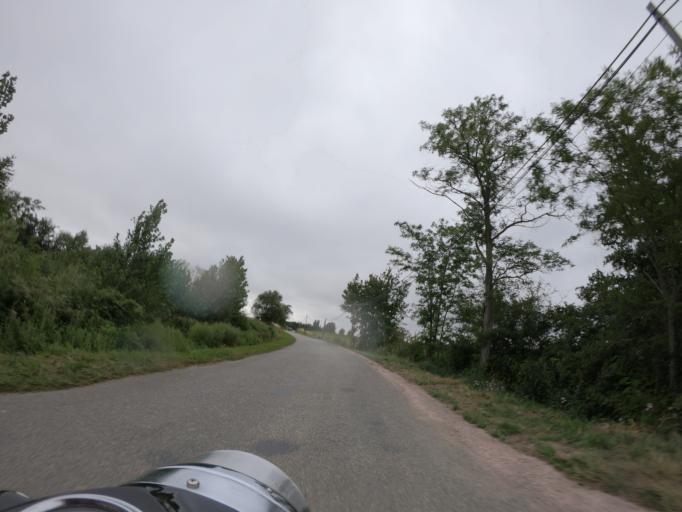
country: FR
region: Midi-Pyrenees
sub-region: Departement de l'Ariege
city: La Tour-du-Crieu
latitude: 43.0973
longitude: 1.7211
